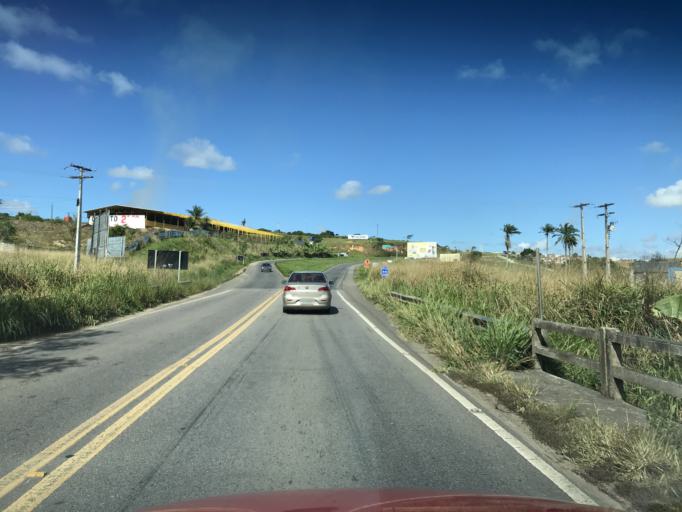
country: BR
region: Bahia
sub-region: Santo Antonio De Jesus
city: Santo Antonio de Jesus
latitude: -12.9475
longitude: -39.2525
